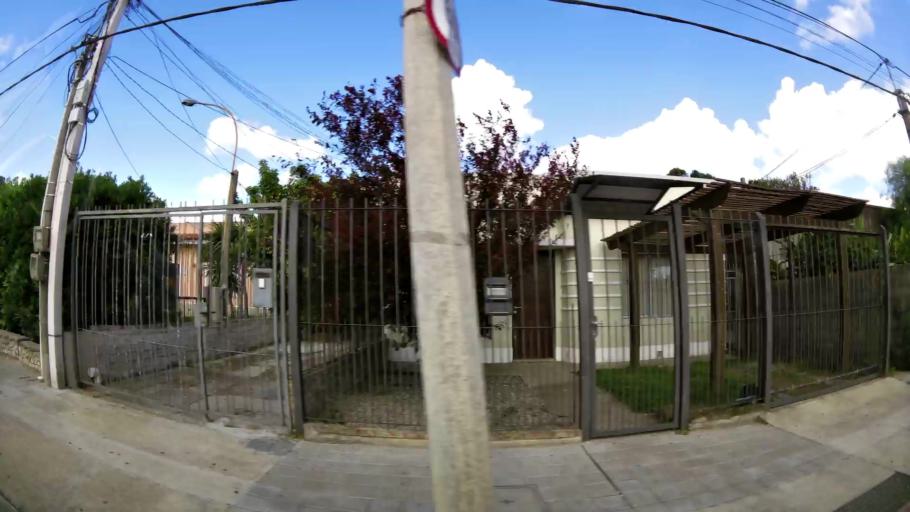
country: UY
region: Canelones
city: La Paz
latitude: -34.8203
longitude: -56.2199
